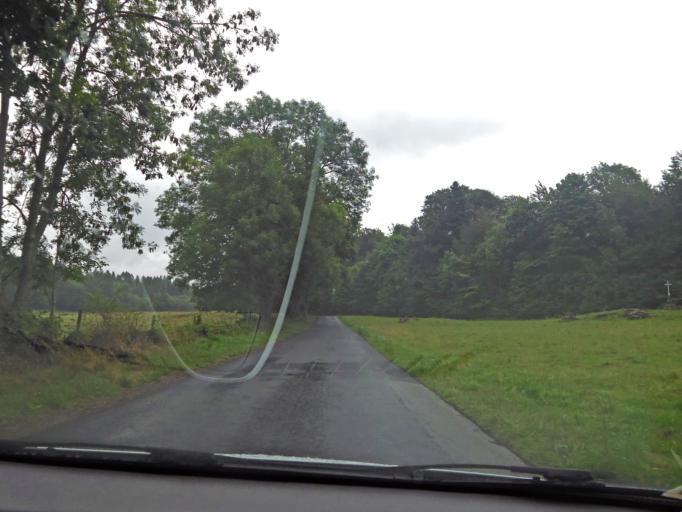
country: FR
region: Auvergne
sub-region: Departement du Puy-de-Dome
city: Orcines
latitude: 45.7514
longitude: 2.9219
